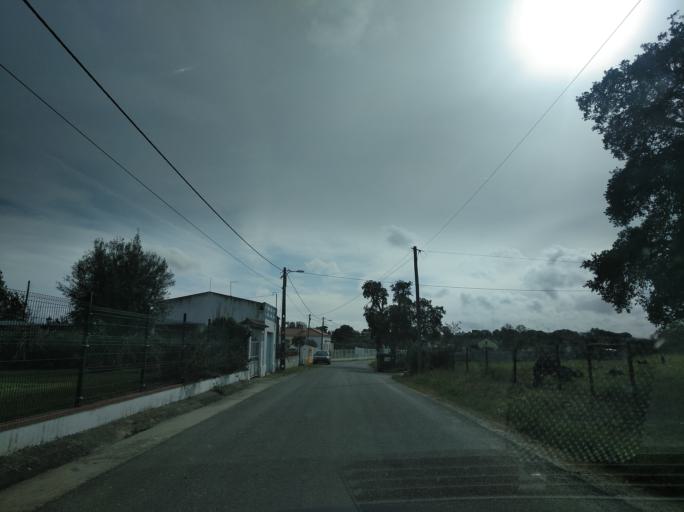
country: PT
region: Setubal
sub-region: Grandola
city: Grandola
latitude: 38.1994
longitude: -8.5460
